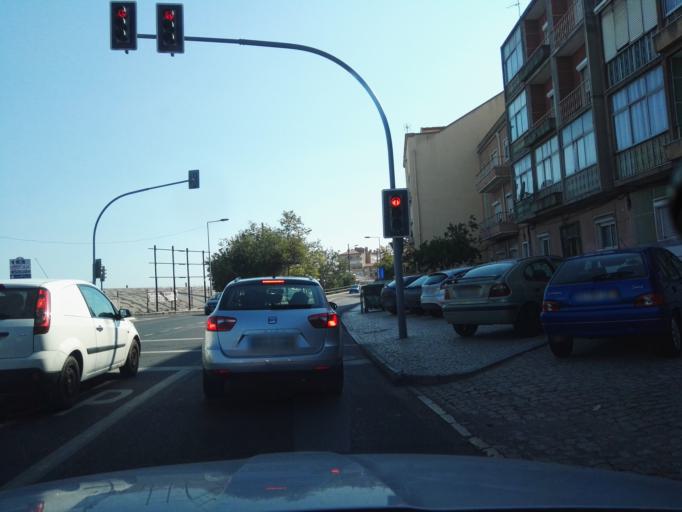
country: PT
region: Lisbon
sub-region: Vila Franca de Xira
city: Povoa de Santa Iria
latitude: 38.8648
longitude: -9.0607
